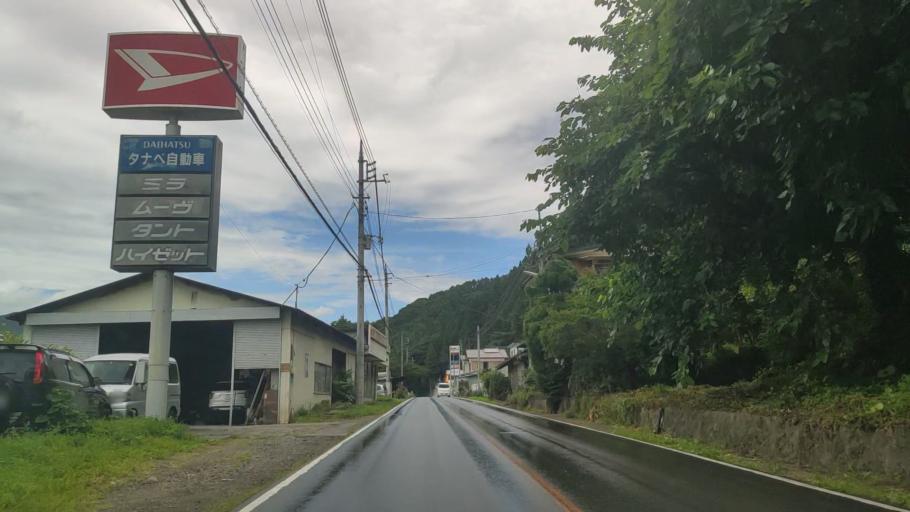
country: JP
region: Gunma
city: Numata
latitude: 36.7439
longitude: 139.2336
